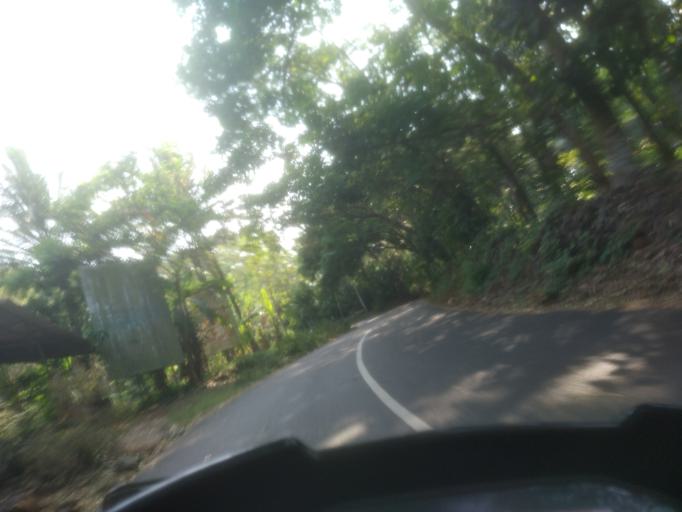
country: IN
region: Kerala
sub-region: Ernakulam
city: Piravam
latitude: 9.8685
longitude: 76.5385
